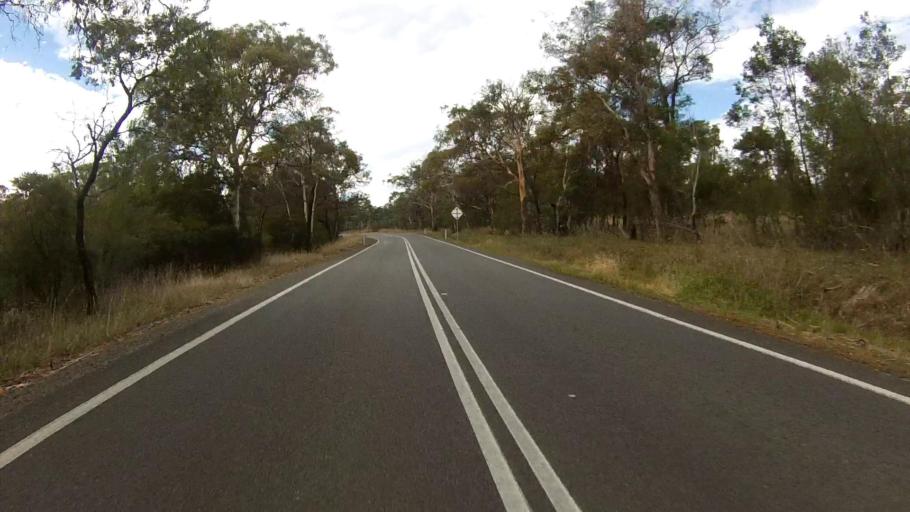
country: AU
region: Tasmania
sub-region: Sorell
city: Sorell
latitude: -42.7014
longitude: 147.4890
